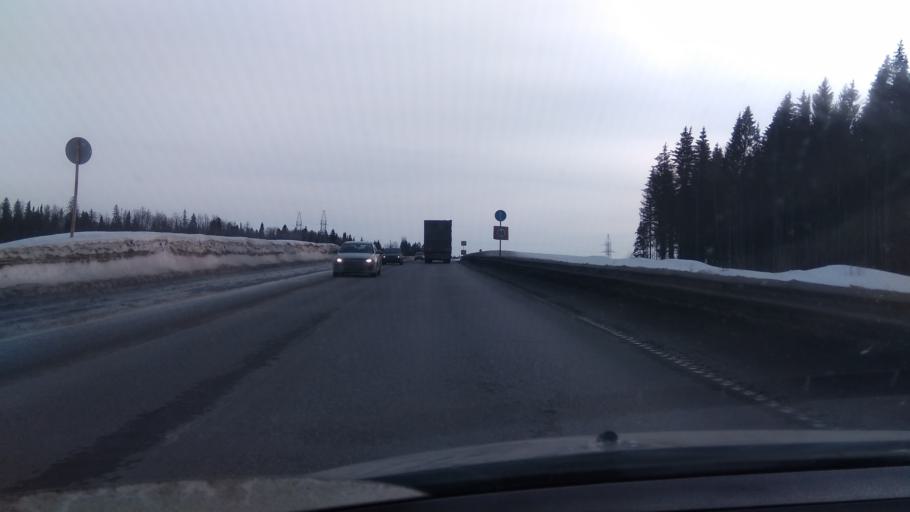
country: RU
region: Perm
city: Ferma
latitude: 57.9537
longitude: 56.3926
